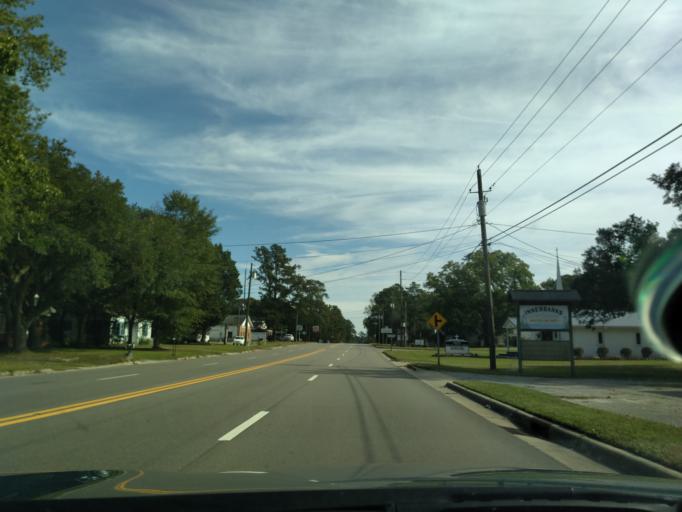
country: US
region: North Carolina
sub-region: Beaufort County
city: Washington
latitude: 35.5329
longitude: -77.0216
